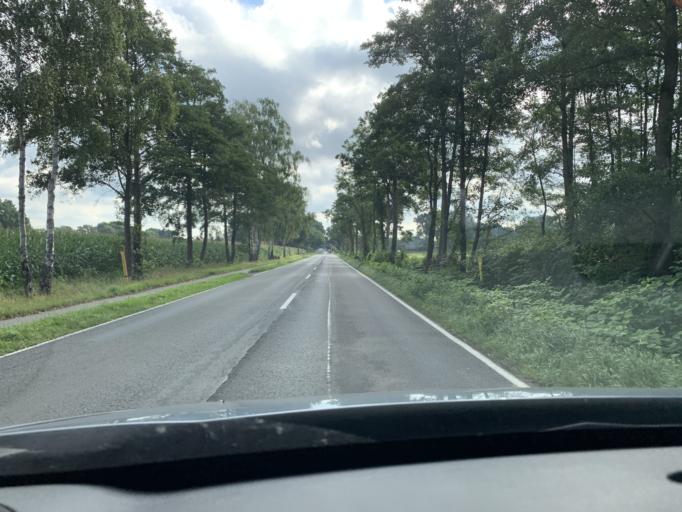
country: DE
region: Lower Saxony
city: Wardenburg
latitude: 53.0715
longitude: 8.1568
